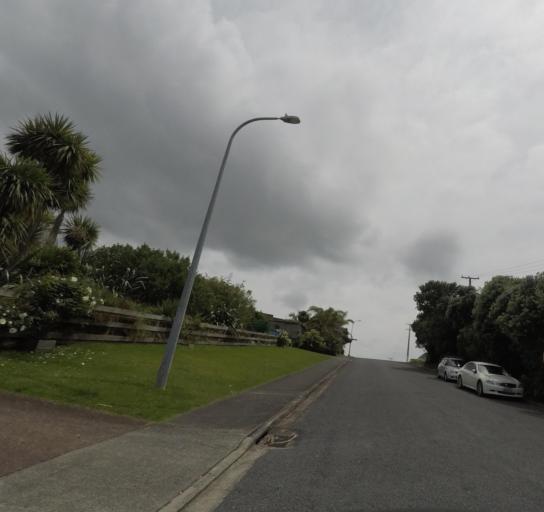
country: NZ
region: Auckland
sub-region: Auckland
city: Warkworth
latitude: -36.2955
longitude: 174.8022
